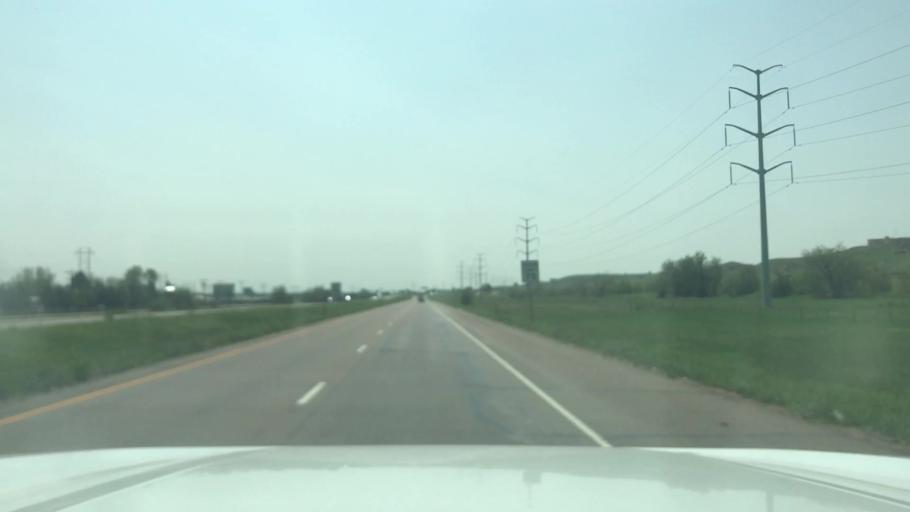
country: US
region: Colorado
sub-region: El Paso County
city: Security-Widefield
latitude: 38.7141
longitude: -104.7268
